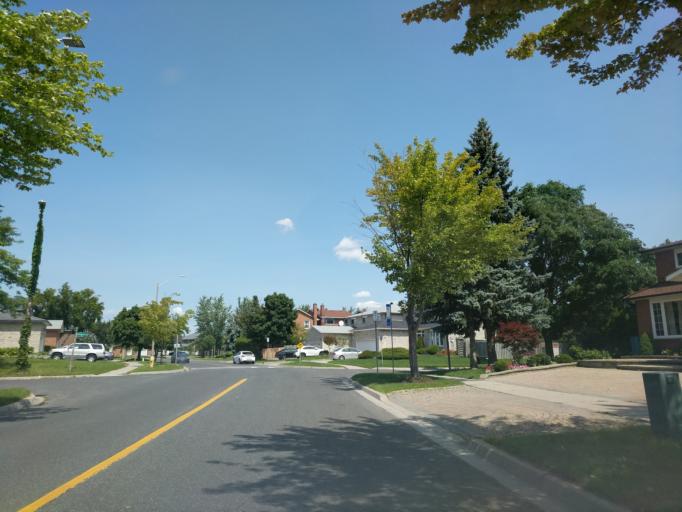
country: CA
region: Ontario
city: Markham
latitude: 43.8261
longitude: -79.3109
